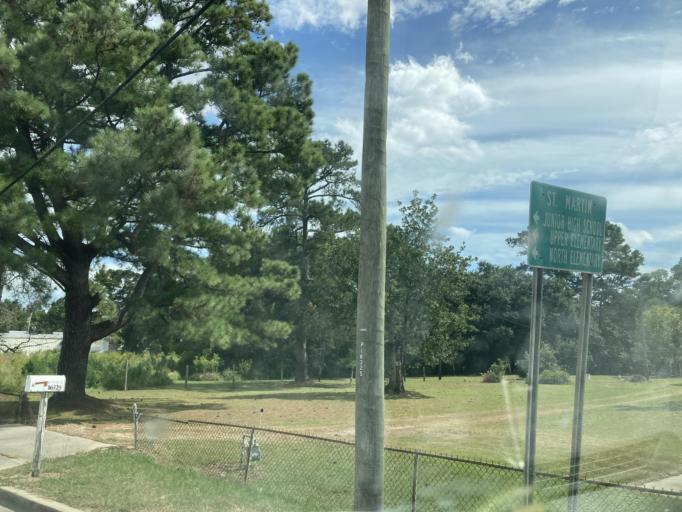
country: US
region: Mississippi
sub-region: Harrison County
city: D'Iberville
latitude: 30.4371
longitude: -88.8832
